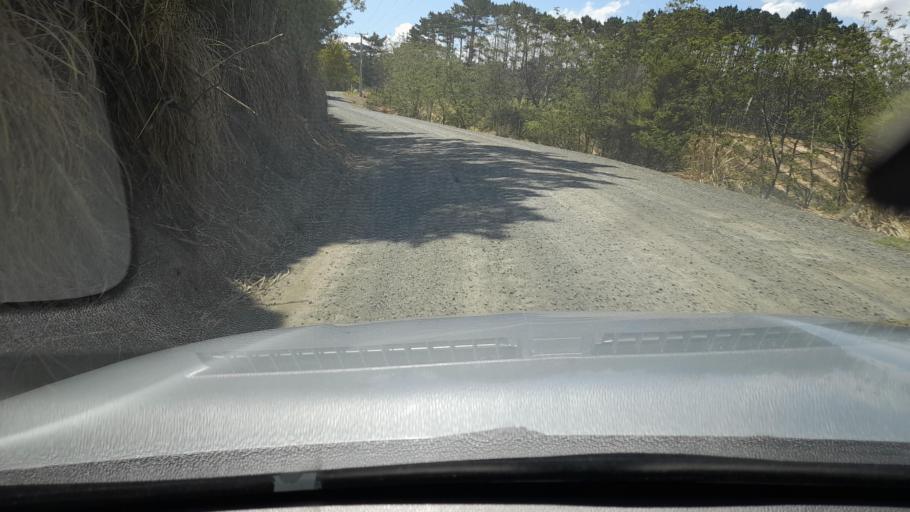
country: NZ
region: Northland
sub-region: Kaipara District
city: Dargaville
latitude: -36.0634
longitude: 173.8777
